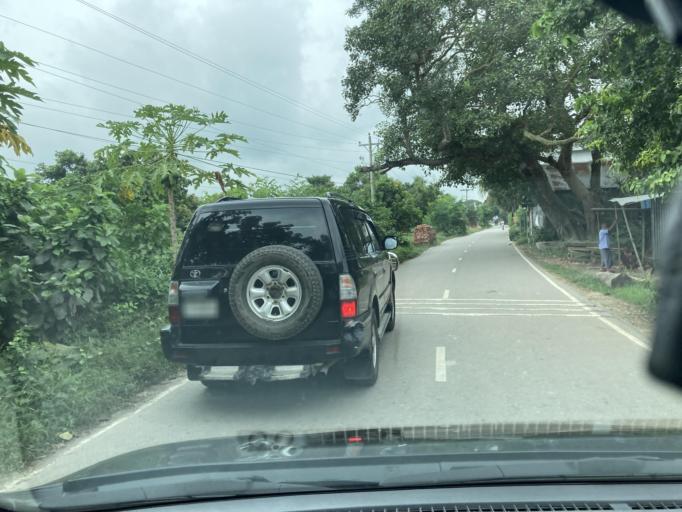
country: BD
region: Dhaka
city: Azimpur
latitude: 23.7700
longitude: 90.2055
